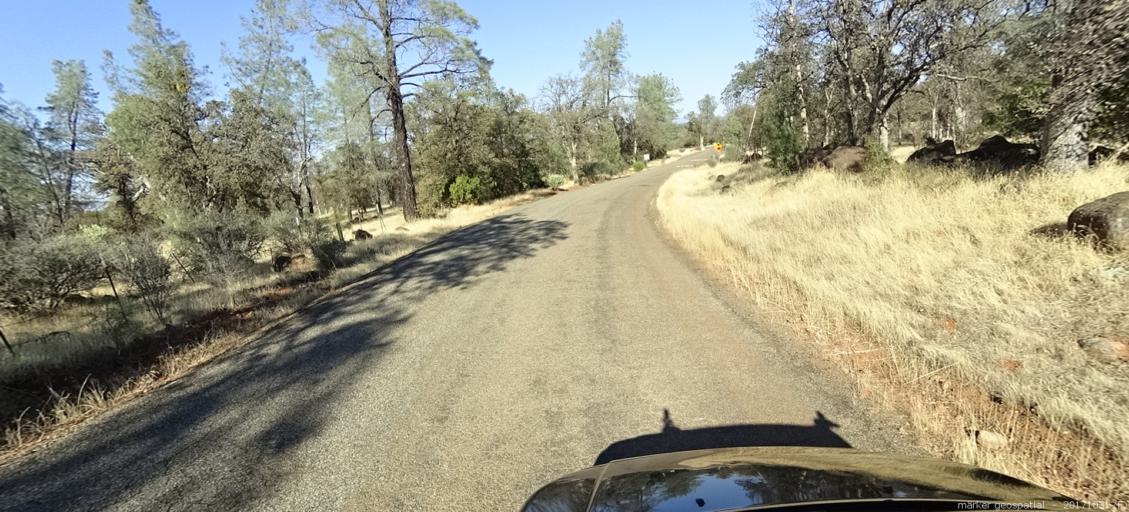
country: US
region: California
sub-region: Shasta County
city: Palo Cedro
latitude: 40.4795
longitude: -122.0846
